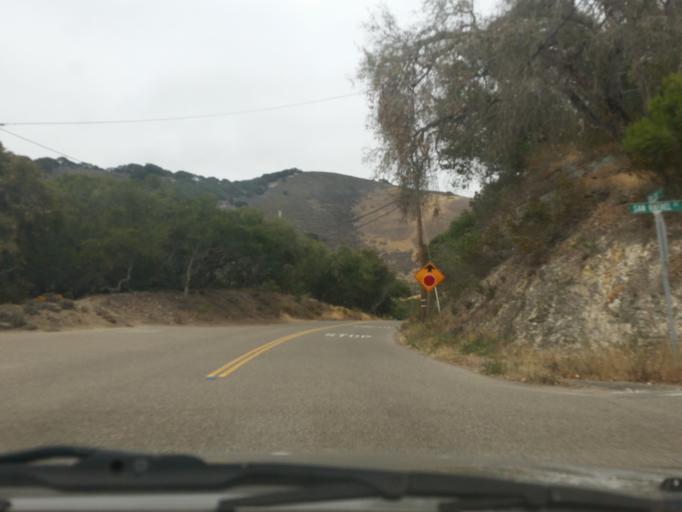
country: US
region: California
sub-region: San Luis Obispo County
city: Avila Beach
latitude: 35.1804
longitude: -120.7294
